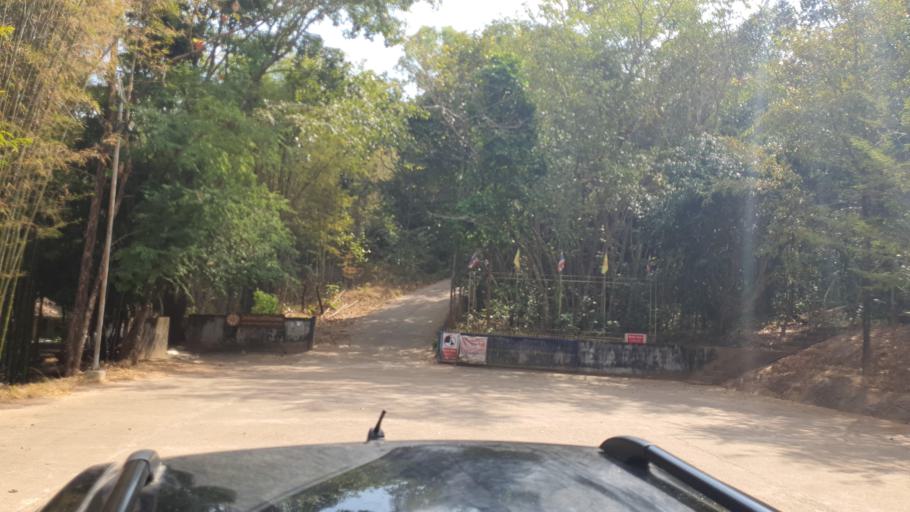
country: TH
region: Changwat Bueng Kan
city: Si Wilai
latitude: 18.2726
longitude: 103.7969
